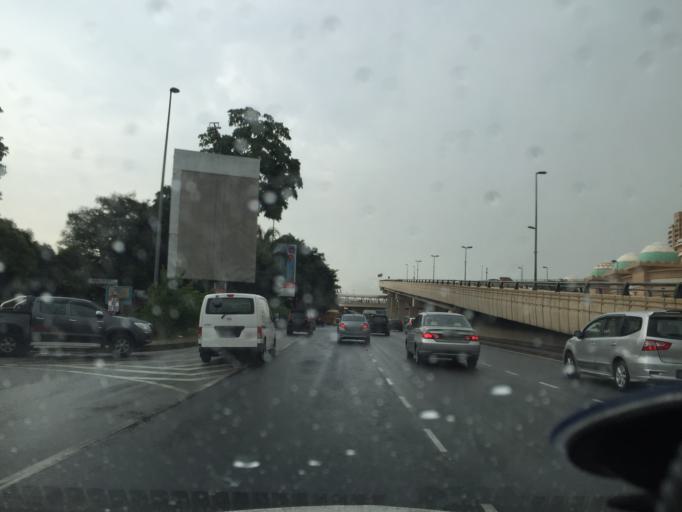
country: MY
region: Selangor
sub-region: Petaling
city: Petaling Jaya
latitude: 3.0738
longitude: 101.6043
